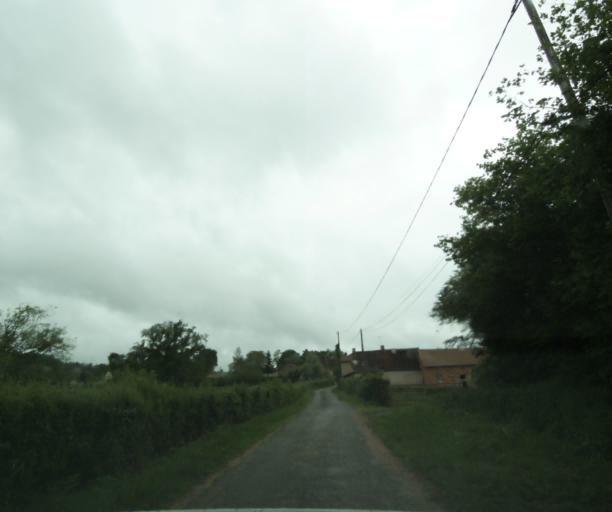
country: FR
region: Bourgogne
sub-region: Departement de Saone-et-Loire
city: Saint-Vallier
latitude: 46.4898
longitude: 4.4672
